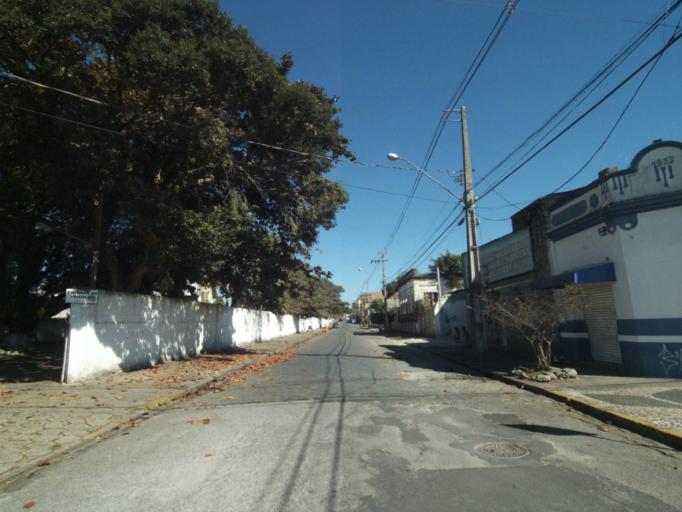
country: BR
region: Parana
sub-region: Paranagua
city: Paranagua
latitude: -25.5157
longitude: -48.5022
